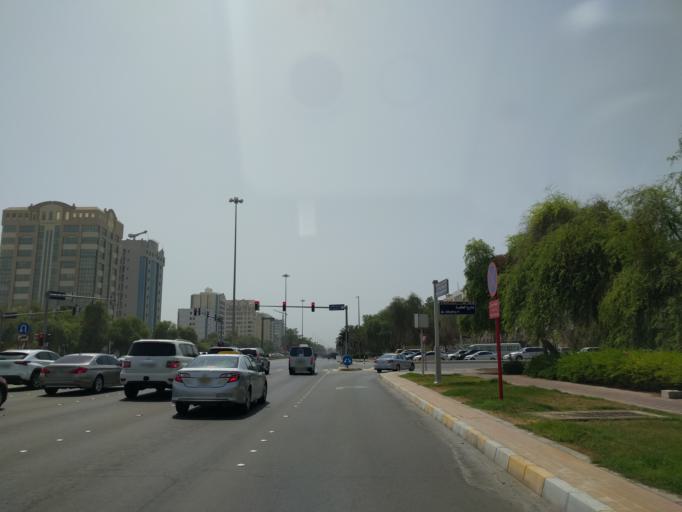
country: AE
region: Abu Dhabi
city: Abu Dhabi
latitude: 24.4377
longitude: 54.4169
